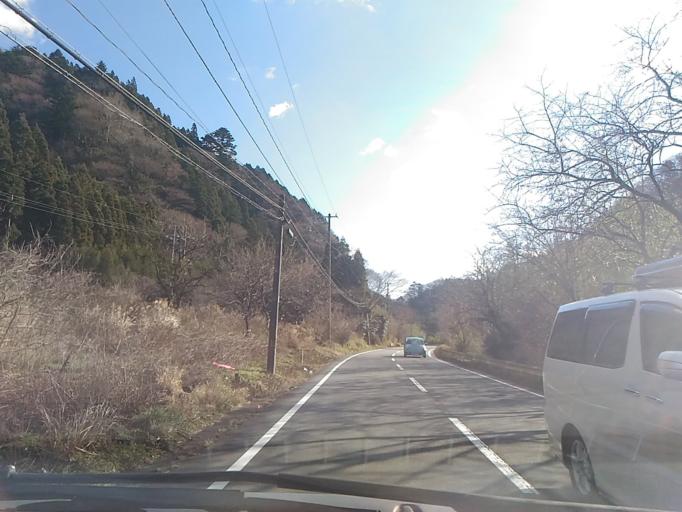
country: JP
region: Fukushima
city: Iwaki
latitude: 37.0253
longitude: 140.6538
